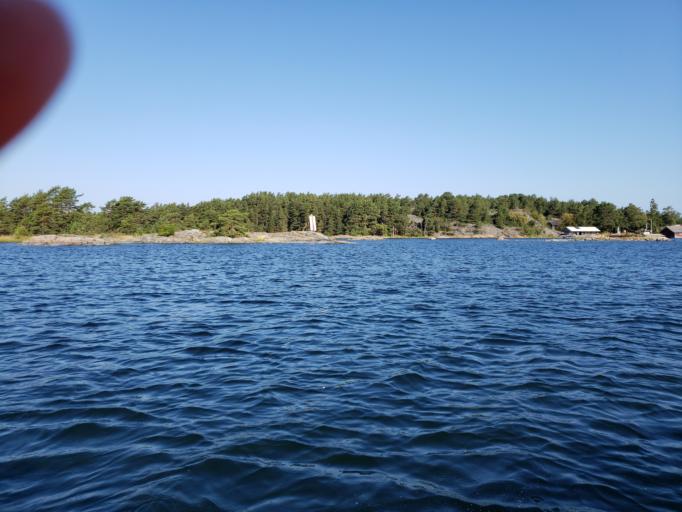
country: FI
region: Varsinais-Suomi
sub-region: Aboland-Turunmaa
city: Dragsfjaerd
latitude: 59.9057
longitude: 22.3675
